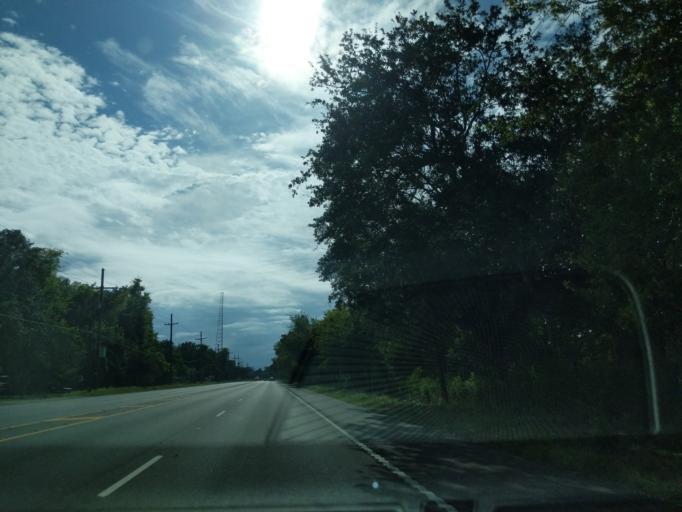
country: US
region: Louisiana
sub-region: Saint Bernard Parish
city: Meraux
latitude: 30.0500
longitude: -89.8841
